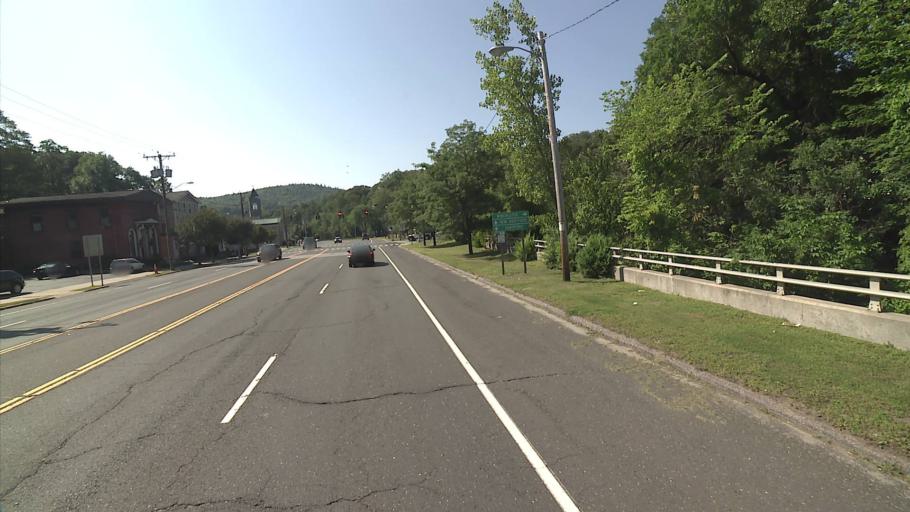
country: US
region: Connecticut
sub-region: Litchfield County
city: Winsted
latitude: 41.9248
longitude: -73.0765
